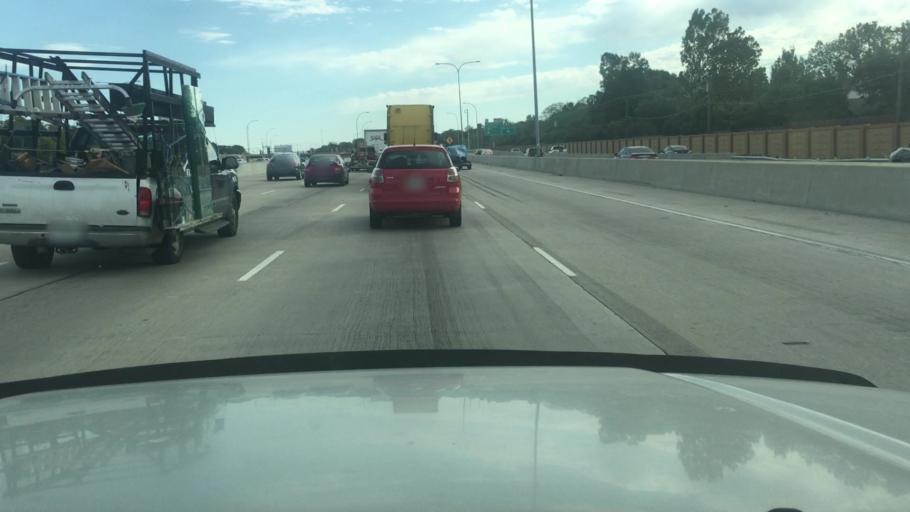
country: US
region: Texas
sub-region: Dallas County
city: Farmers Branch
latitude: 32.9157
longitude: -96.8623
